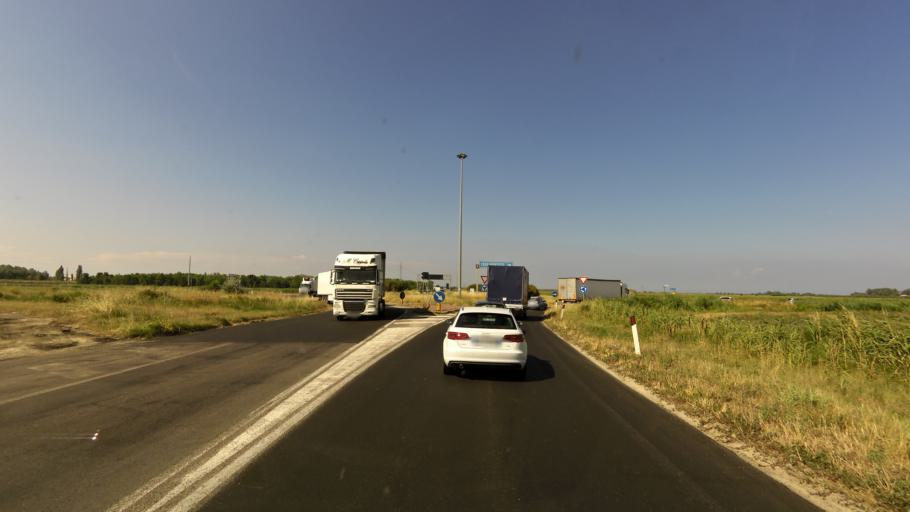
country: IT
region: Emilia-Romagna
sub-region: Provincia di Ravenna
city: Marina Romea
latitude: 44.5653
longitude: 12.2506
